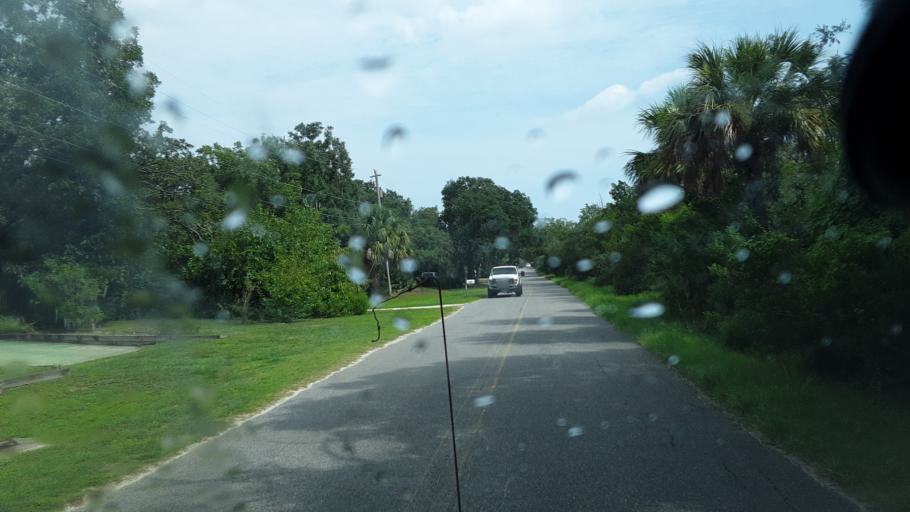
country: US
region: Georgia
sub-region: Chatham County
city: Tybee Island
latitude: 32.0147
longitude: -80.8690
